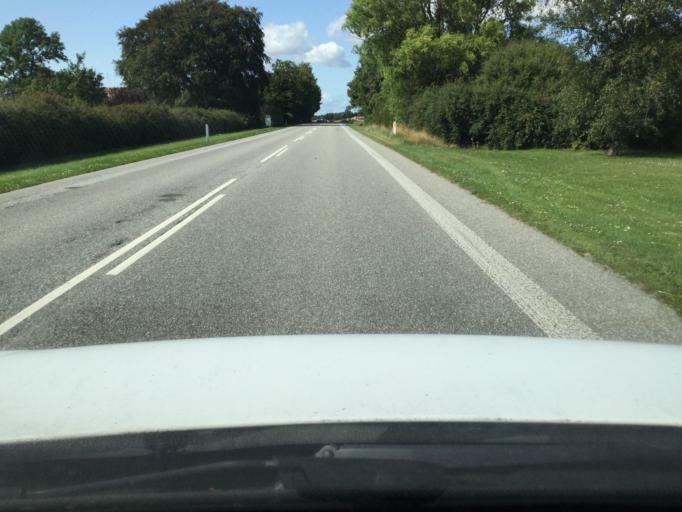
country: DK
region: Zealand
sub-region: Lolland Kommune
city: Rodby
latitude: 54.7791
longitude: 11.2973
